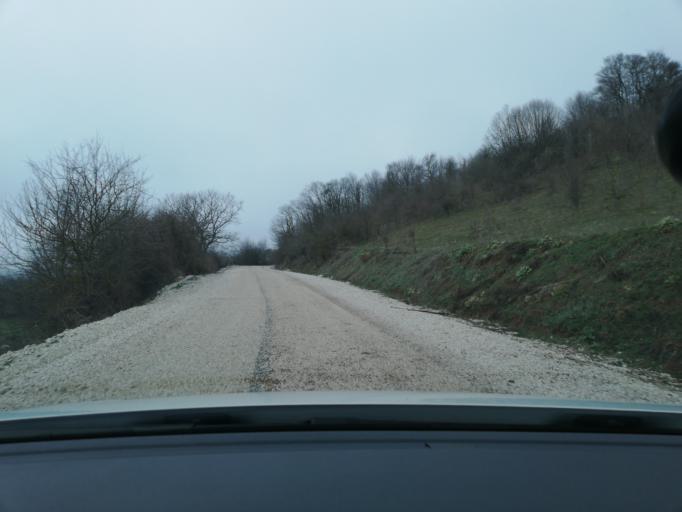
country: TR
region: Bolu
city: Bolu
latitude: 40.6611
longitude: 31.4659
